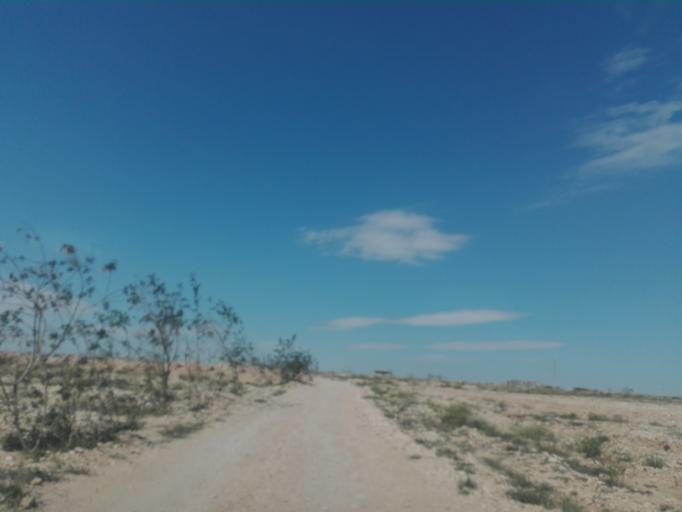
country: TN
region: Safaqis
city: Sfax
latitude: 34.6877
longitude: 10.5417
